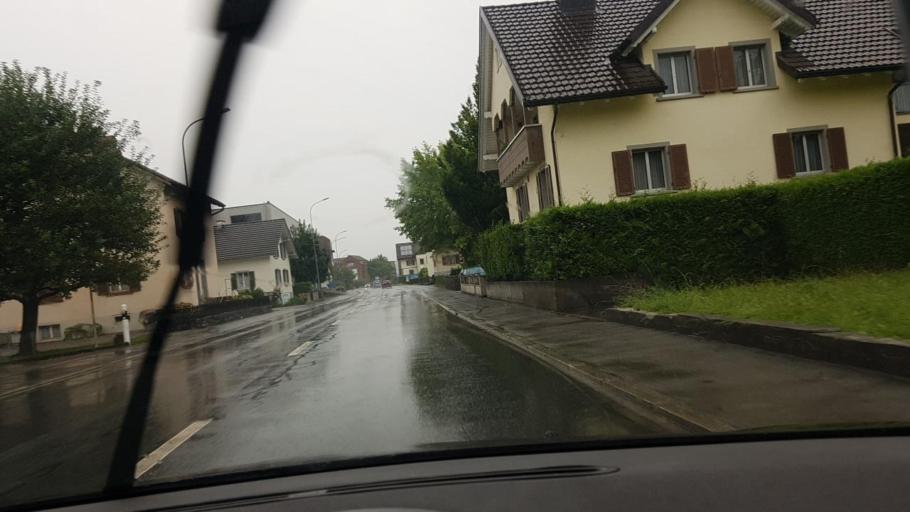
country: LI
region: Triesen
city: Triesen
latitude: 47.1119
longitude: 9.5241
